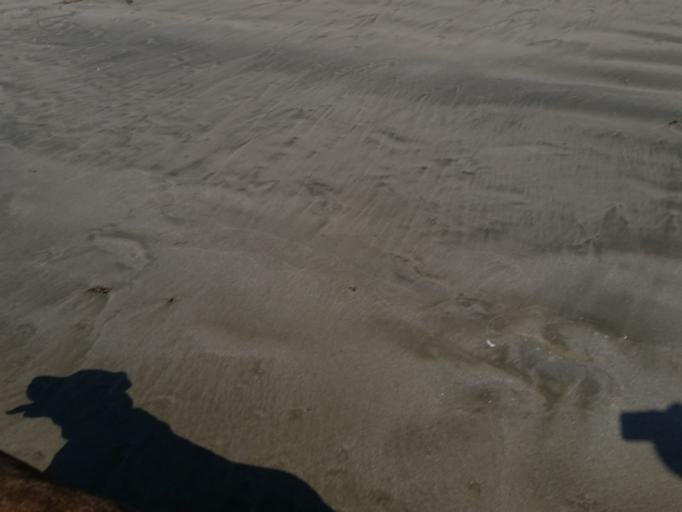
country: NI
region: Managua
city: Masachapa
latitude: 11.7842
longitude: -86.5178
